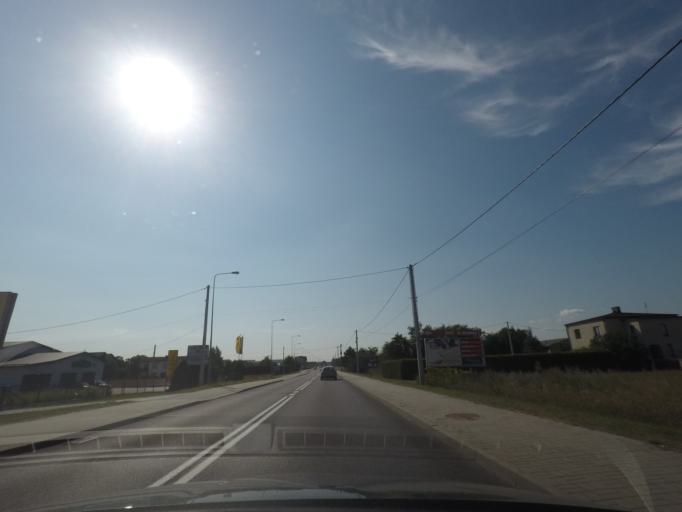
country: PL
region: Silesian Voivodeship
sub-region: Powiat pszczynski
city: Rudziczka
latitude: 50.0395
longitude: 18.7315
